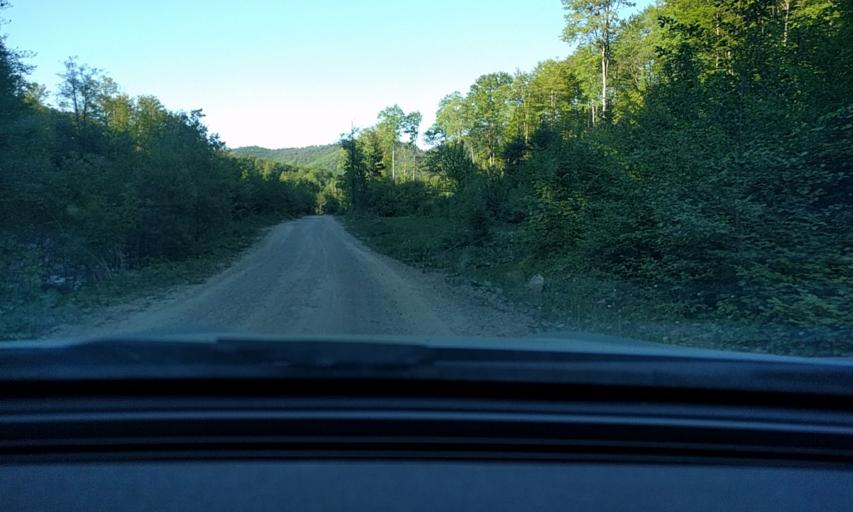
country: RO
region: Bacau
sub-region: Comuna Oituz
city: Ferestrau-Oituz
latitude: 46.1694
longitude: 26.5736
